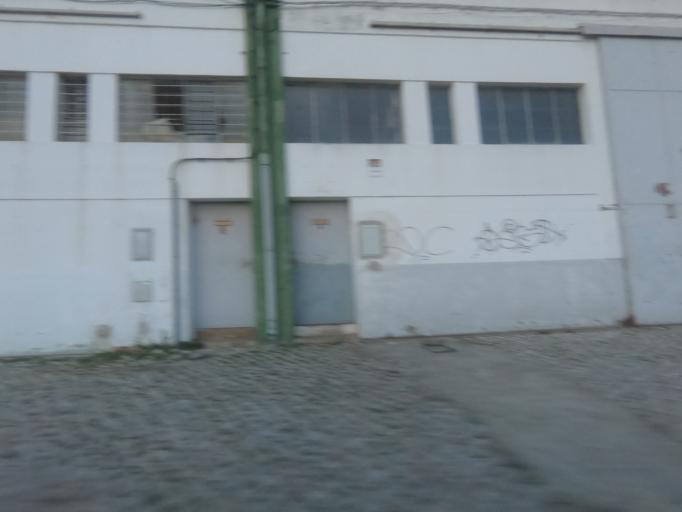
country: PT
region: Setubal
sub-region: Setubal
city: Setubal
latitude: 38.5170
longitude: -8.8701
